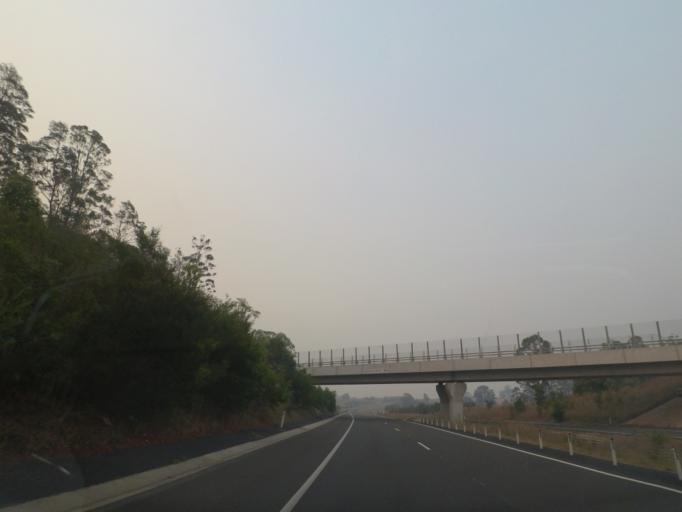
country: AU
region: New South Wales
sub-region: Nambucca Shire
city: Macksville
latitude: -30.7646
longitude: 152.9039
